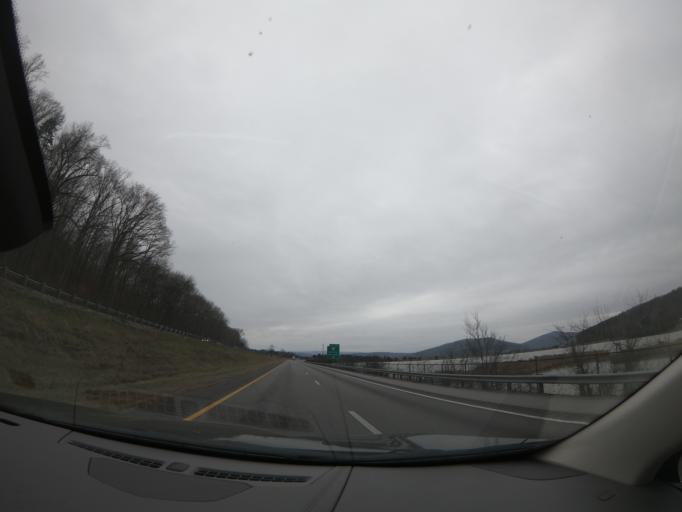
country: US
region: Tennessee
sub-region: Marion County
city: Jasper
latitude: 35.0127
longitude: -85.5344
